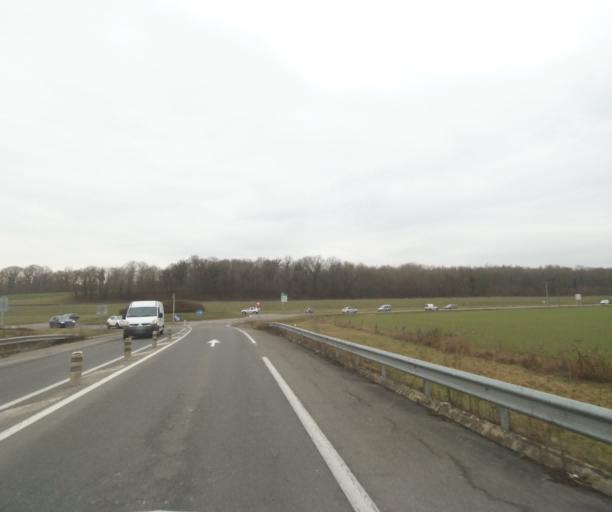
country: FR
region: Champagne-Ardenne
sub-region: Departement de la Haute-Marne
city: Saint-Dizier
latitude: 48.6234
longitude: 4.9366
